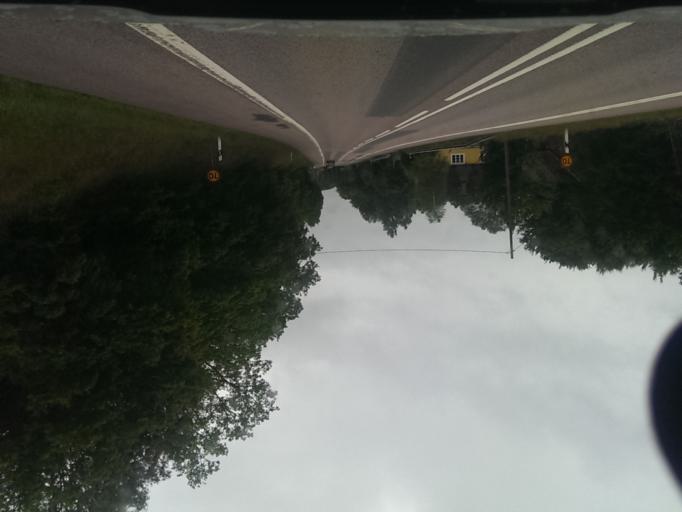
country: SE
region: Skane
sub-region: Orkelljunga Kommun
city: OErkelljunga
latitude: 56.2906
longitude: 13.3277
